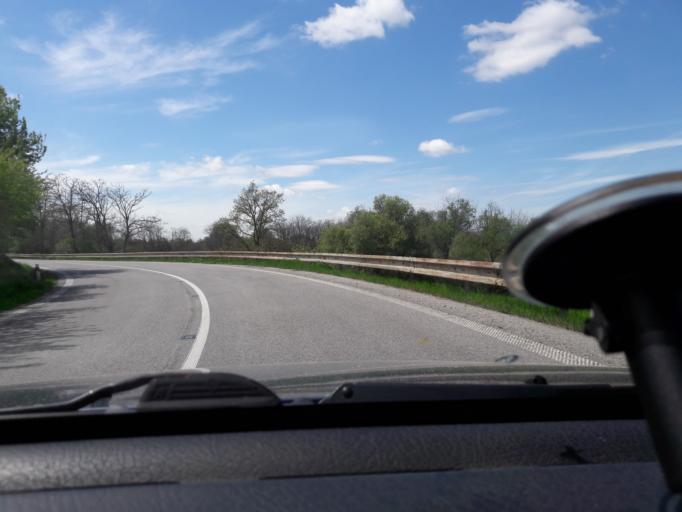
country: SK
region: Nitriansky
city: Levice
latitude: 48.2595
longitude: 18.7537
